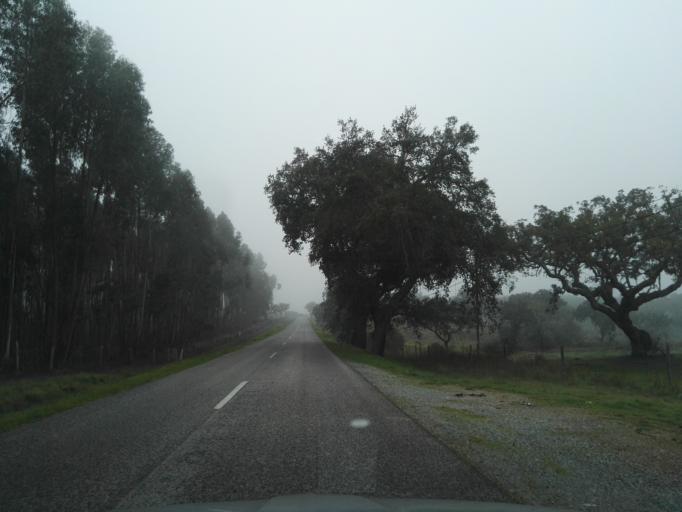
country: PT
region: Evora
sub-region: Montemor-O-Novo
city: Montemor-o-Novo
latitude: 38.7801
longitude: -8.2151
